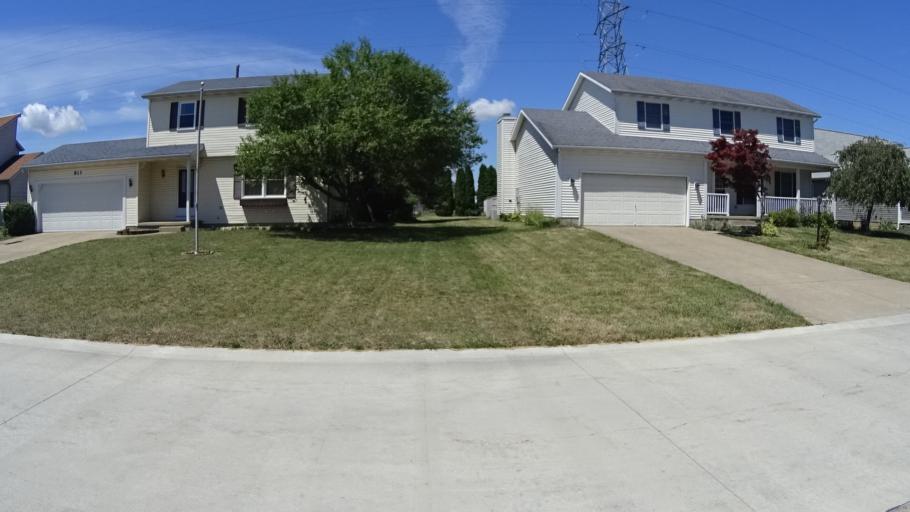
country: US
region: Ohio
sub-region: Erie County
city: Sandusky
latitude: 41.4038
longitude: -82.6924
